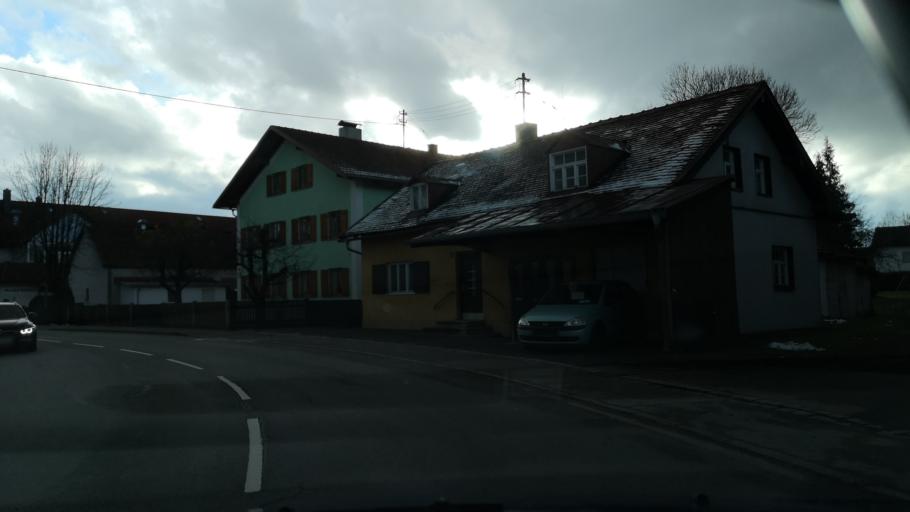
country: DE
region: Bavaria
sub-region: Upper Bavaria
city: Kirchheim bei Muenchen
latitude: 48.1878
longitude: 11.7749
